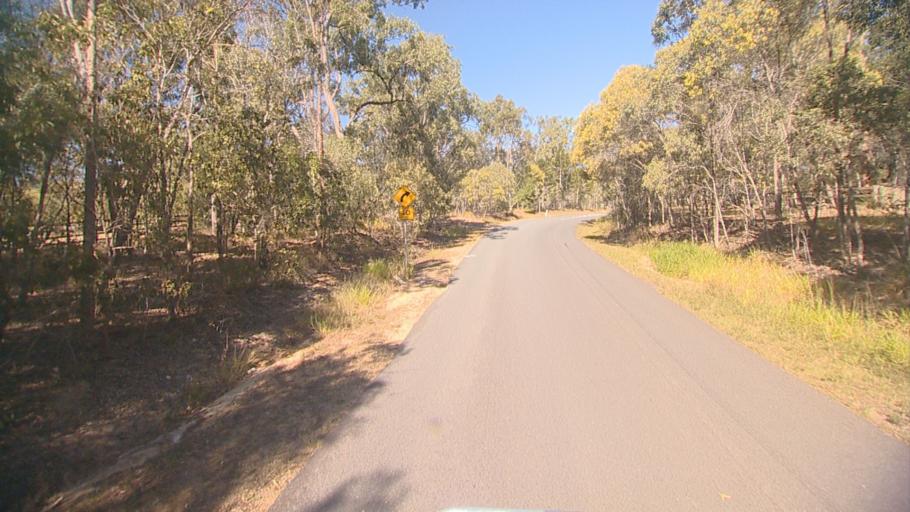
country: AU
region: Queensland
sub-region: Ipswich
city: Springfield Lakes
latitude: -27.7100
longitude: 152.9349
